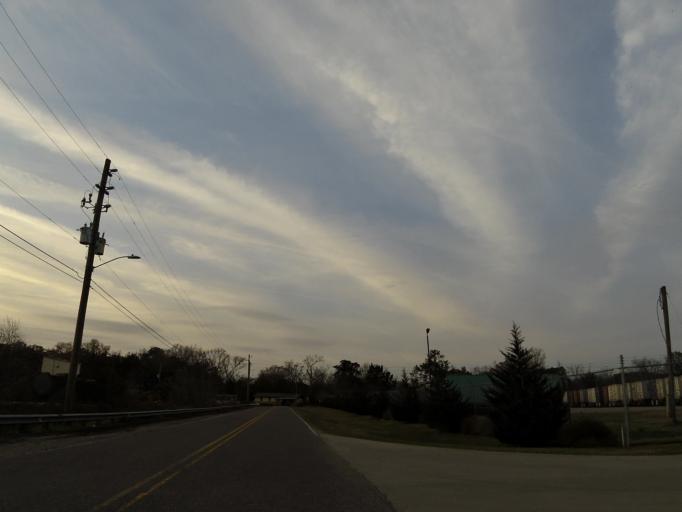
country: US
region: Florida
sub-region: Duval County
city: Jacksonville
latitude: 30.3660
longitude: -81.7160
